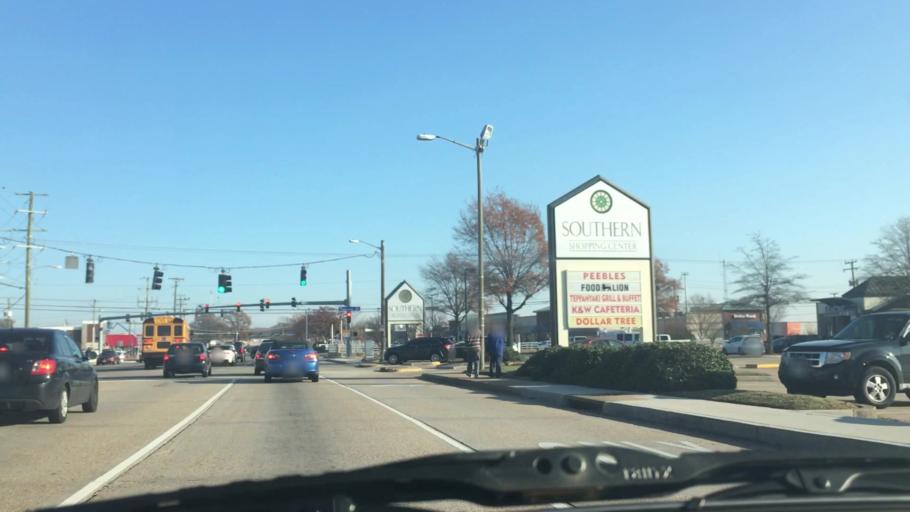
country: US
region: Virginia
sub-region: City of Norfolk
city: Norfolk
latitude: 36.9165
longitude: -76.2552
